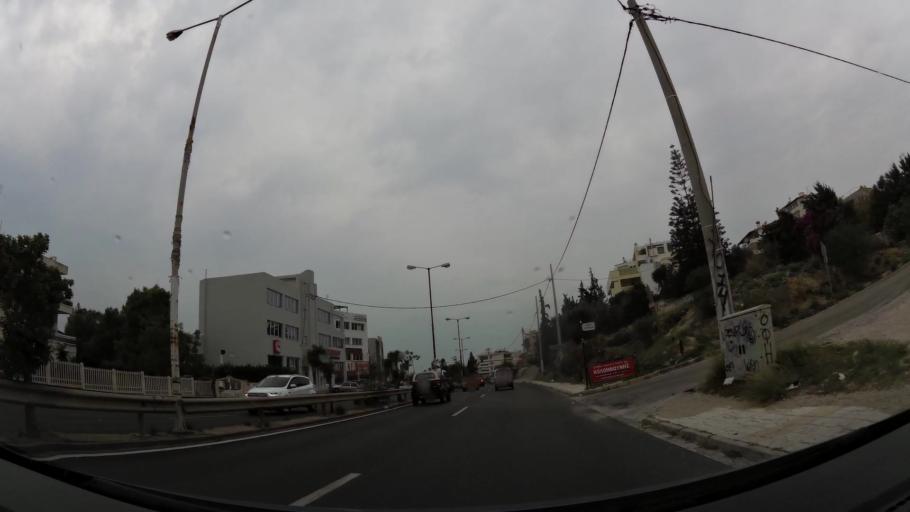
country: GR
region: Attica
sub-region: Nomarchia Athinas
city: Alimos
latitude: 37.9076
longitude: 23.7305
